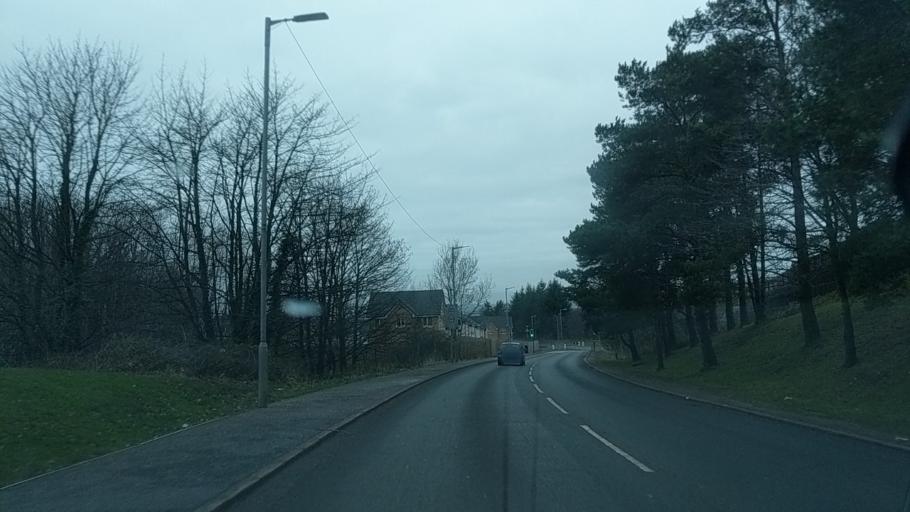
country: GB
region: Scotland
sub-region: South Lanarkshire
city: Rutherglen
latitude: 55.8107
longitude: -4.1848
